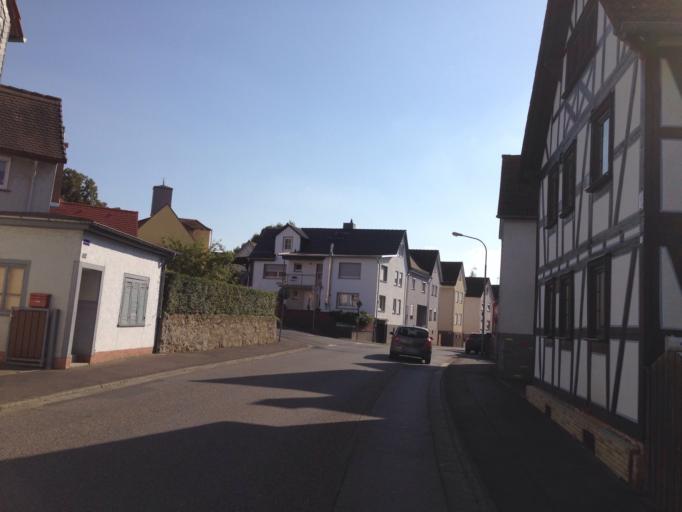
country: DE
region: Hesse
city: Staufenberg
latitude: 50.6504
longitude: 8.7377
